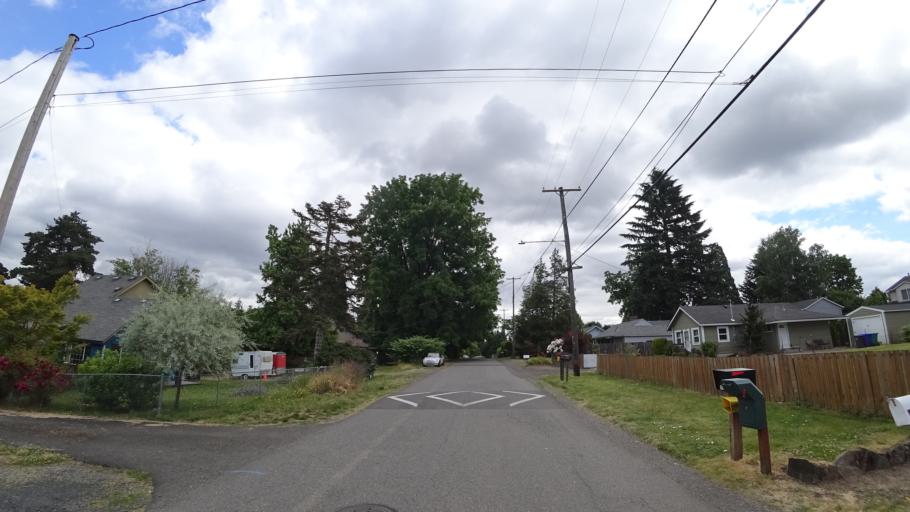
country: US
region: Oregon
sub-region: Multnomah County
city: Portland
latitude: 45.5651
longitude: -122.6080
